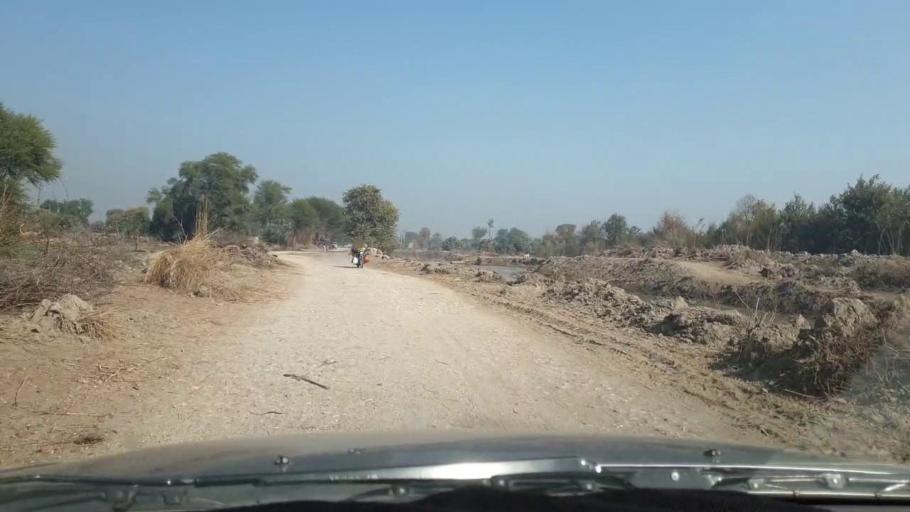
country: PK
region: Sindh
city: Khanpur
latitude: 27.7756
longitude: 69.5377
